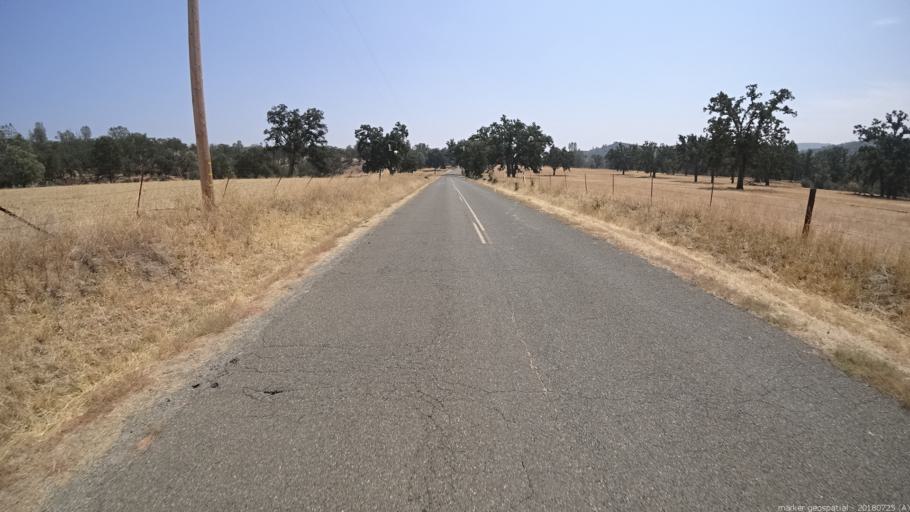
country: US
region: California
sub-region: Fresno County
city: Coalinga
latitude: 35.9198
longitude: -120.4906
